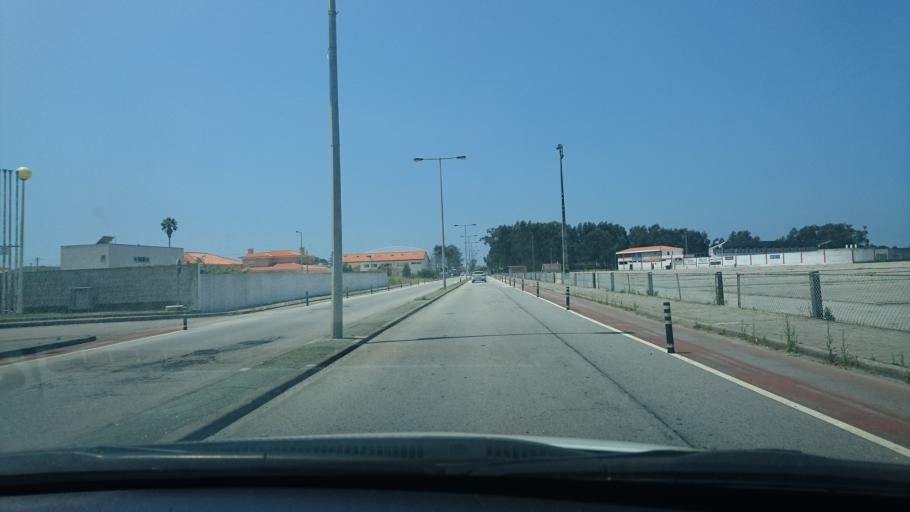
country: PT
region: Aveiro
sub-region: Ovar
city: Esmoriz
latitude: 40.9571
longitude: -8.6402
